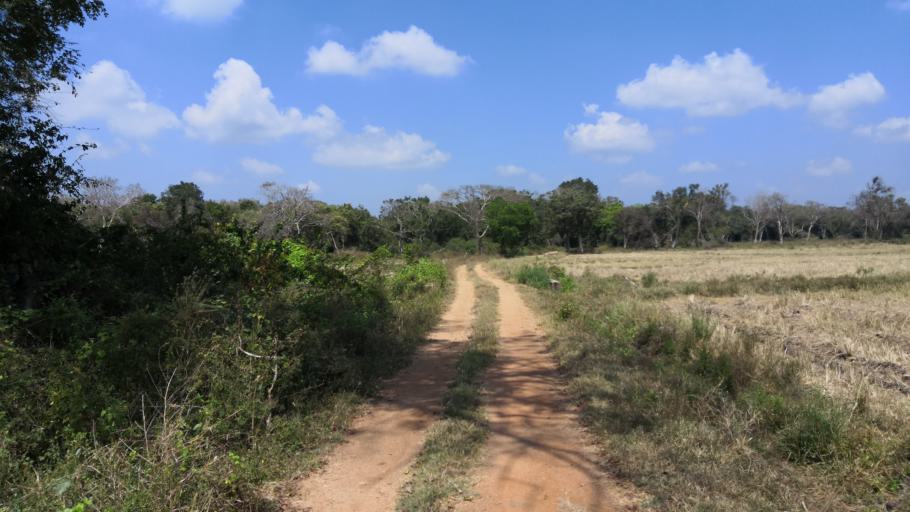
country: LK
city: Padaviya Divisional Secretariat
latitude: 8.9633
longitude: 80.6918
